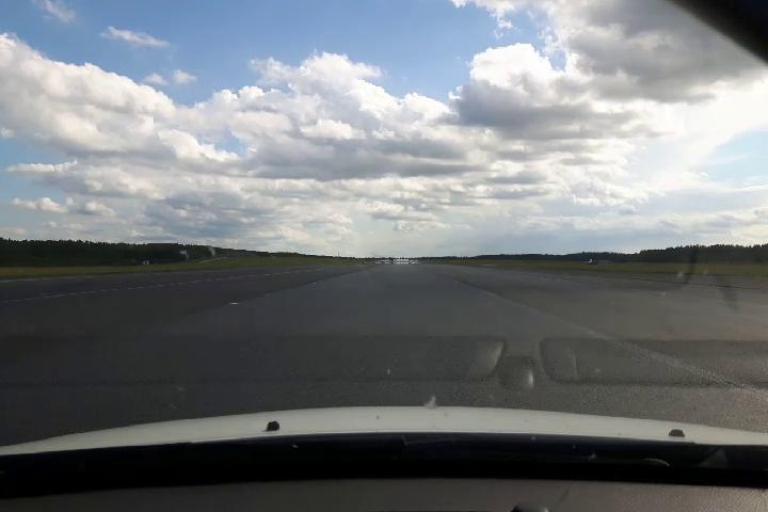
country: SE
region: Stockholm
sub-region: Sigtuna Kommun
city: Rosersberg
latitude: 59.6397
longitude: 17.9554
